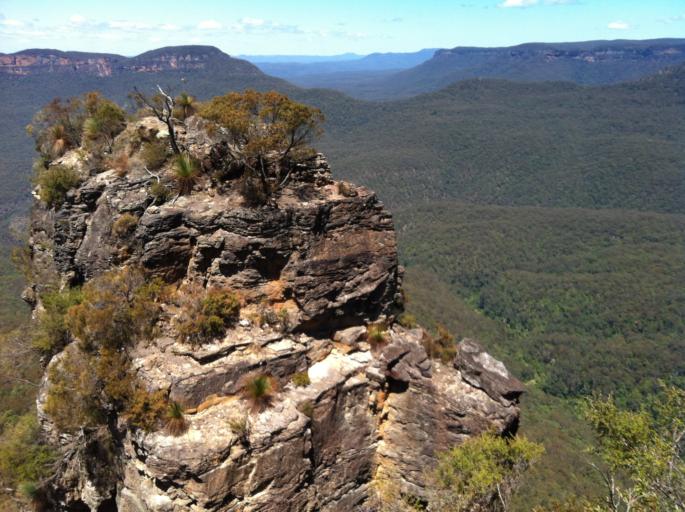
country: AU
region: New South Wales
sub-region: Blue Mountains Municipality
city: Katoomba
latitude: -33.7348
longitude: 150.3148
